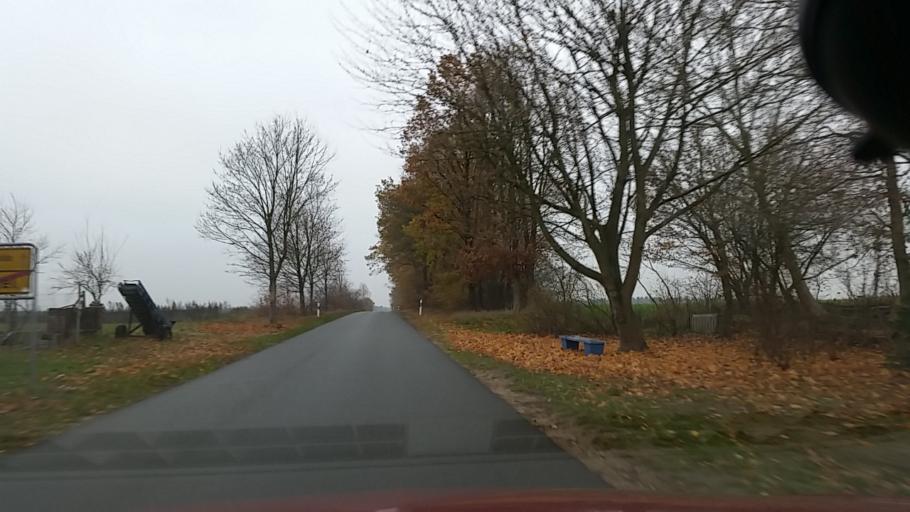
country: DE
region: Lower Saxony
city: Stadensen
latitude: 52.8116
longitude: 10.5471
